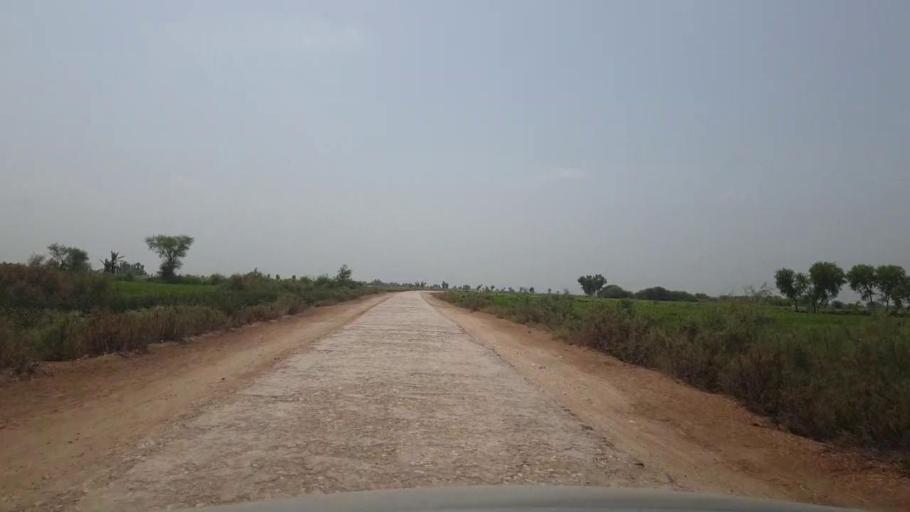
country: PK
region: Sindh
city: Garhi Yasin
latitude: 27.9413
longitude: 68.3889
